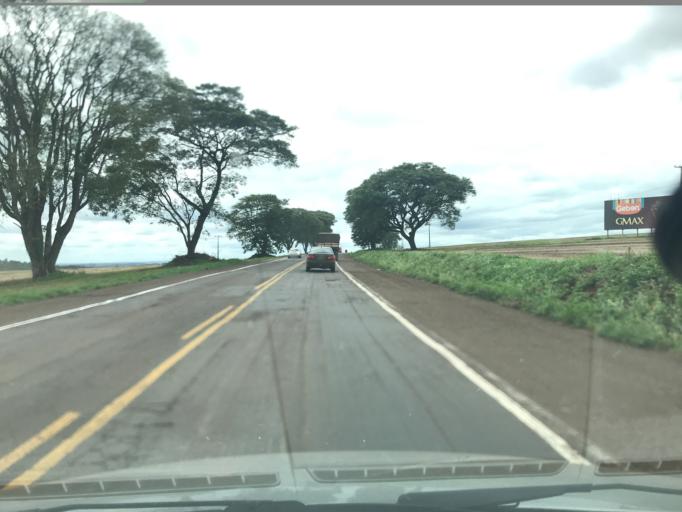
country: BR
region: Parana
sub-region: Terra Boa
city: Terra Boa
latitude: -23.6059
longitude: -52.4148
